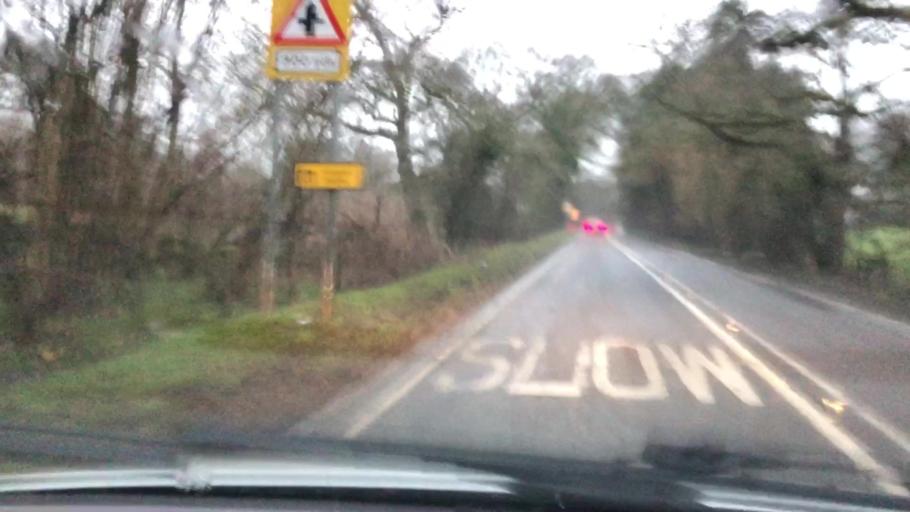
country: GB
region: England
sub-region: Hampshire
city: Alton
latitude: 51.1821
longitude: -0.9884
